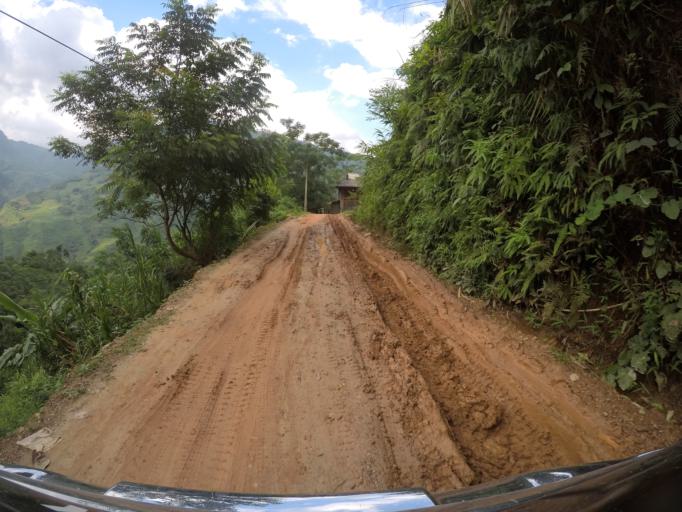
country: VN
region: Yen Bai
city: Son Thinh
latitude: 21.6811
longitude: 104.5778
